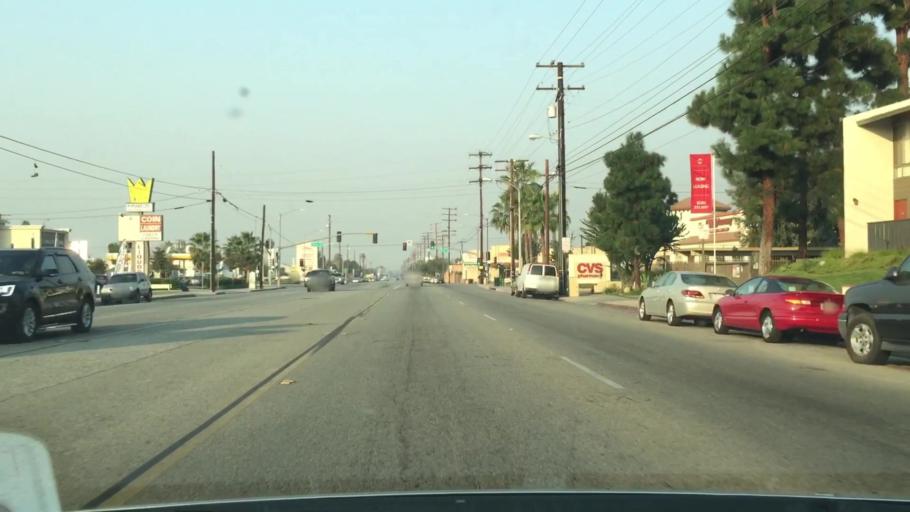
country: US
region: California
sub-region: Los Angeles County
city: Citrus
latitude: 34.1068
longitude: -117.8889
